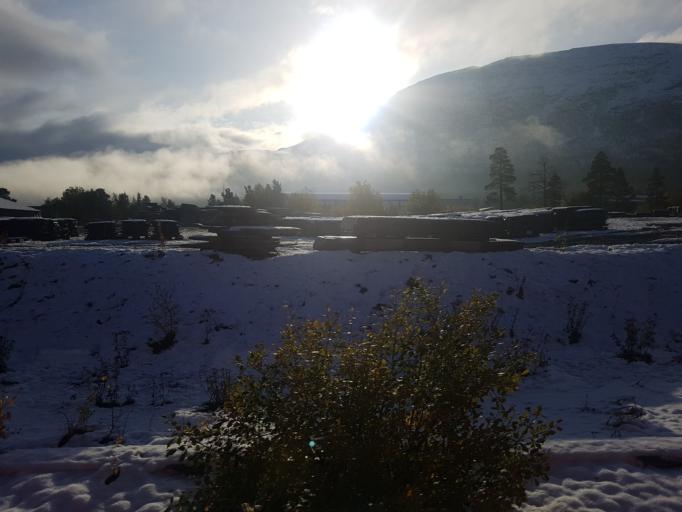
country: NO
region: Sor-Trondelag
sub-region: Oppdal
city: Oppdal
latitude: 62.5972
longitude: 9.6774
